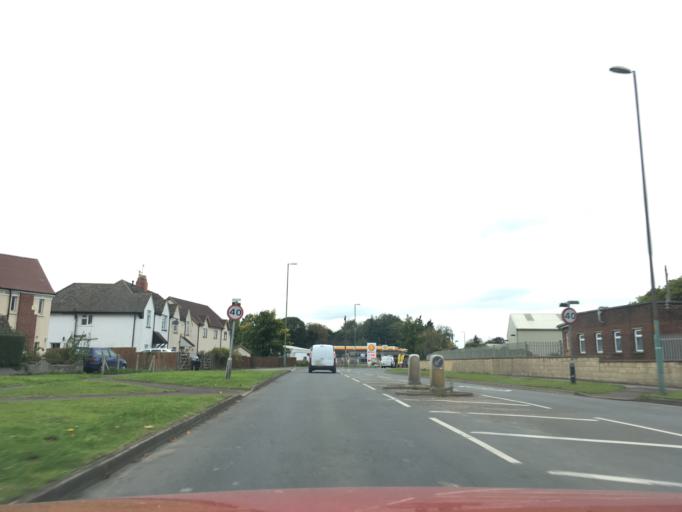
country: GB
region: England
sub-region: Gloucestershire
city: Dursley
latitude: 51.7083
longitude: -2.3654
